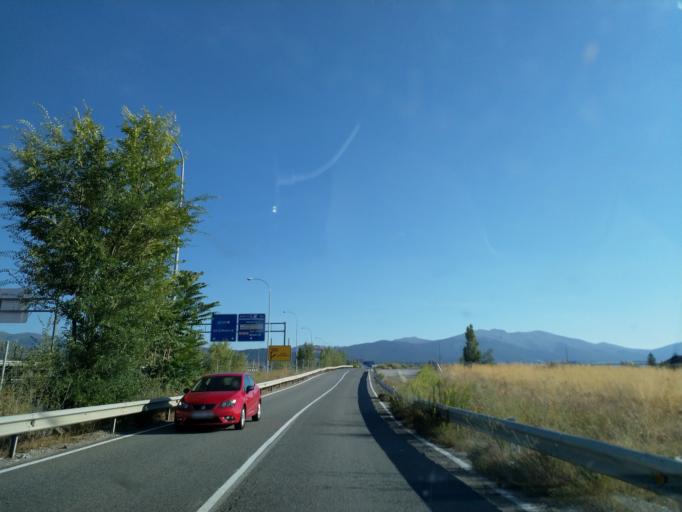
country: ES
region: Castille and Leon
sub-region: Provincia de Segovia
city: Segovia
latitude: 40.9157
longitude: -4.1055
